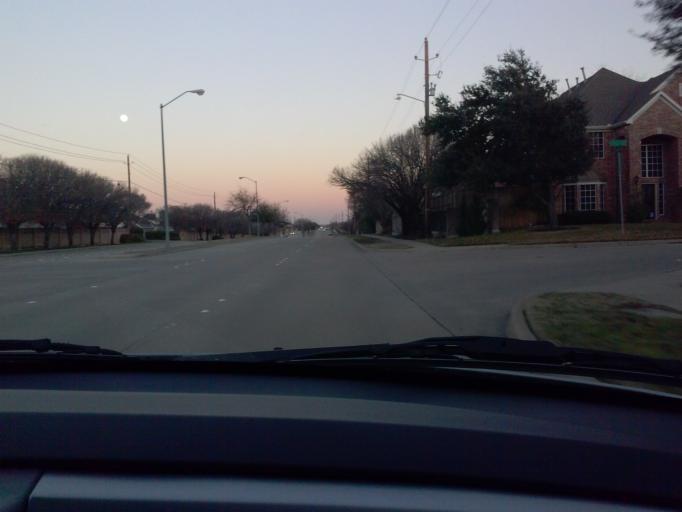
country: US
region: Texas
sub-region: Collin County
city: Allen
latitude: 33.0860
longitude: -96.7472
